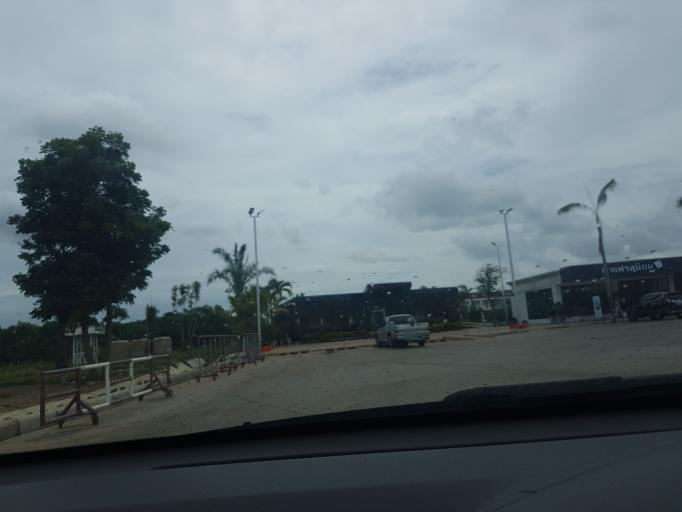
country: TH
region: Lampang
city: Ko Kha
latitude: 18.2340
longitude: 99.4345
